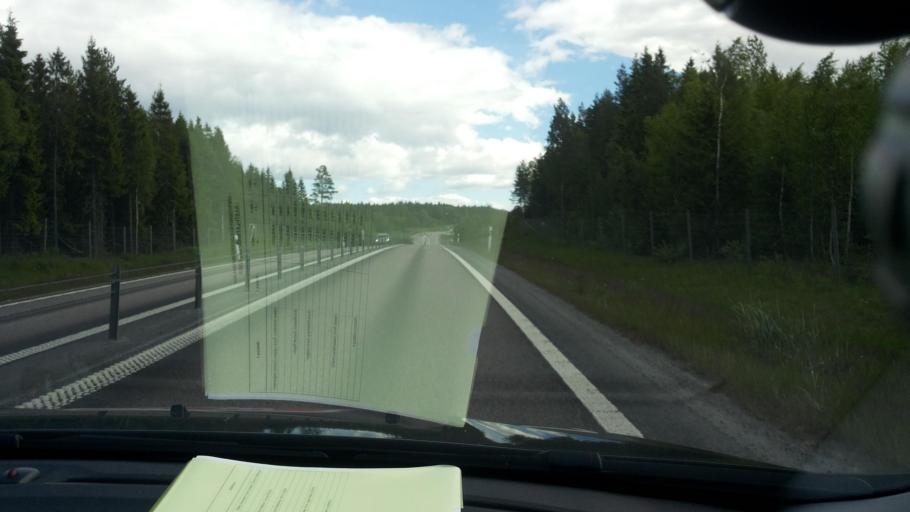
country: SE
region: Vaesternorrland
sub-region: Timra Kommun
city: Soraker
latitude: 62.5412
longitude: 17.5669
